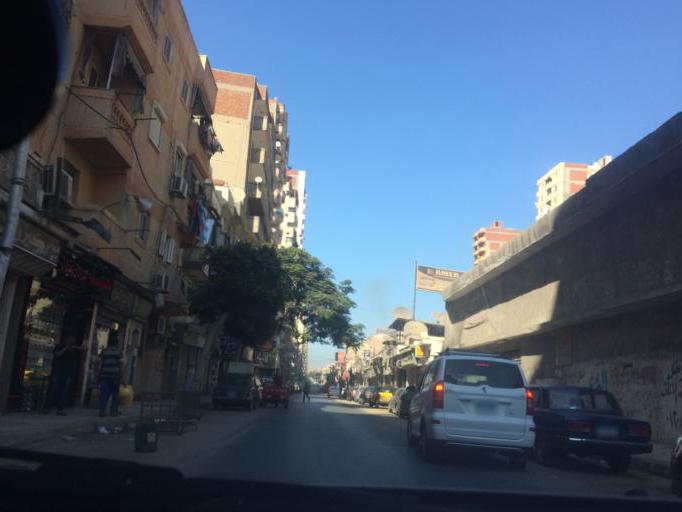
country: EG
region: Alexandria
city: Alexandria
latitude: 31.2501
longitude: 29.9820
